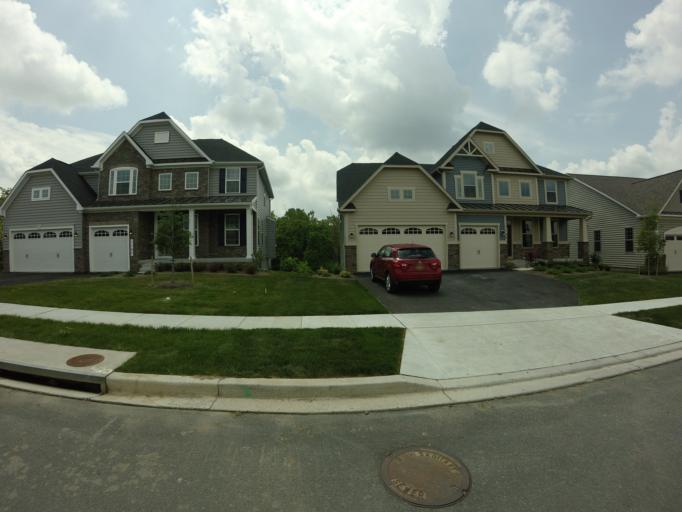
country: US
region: Maryland
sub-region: Frederick County
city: Brunswick
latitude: 39.3248
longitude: -77.6329
